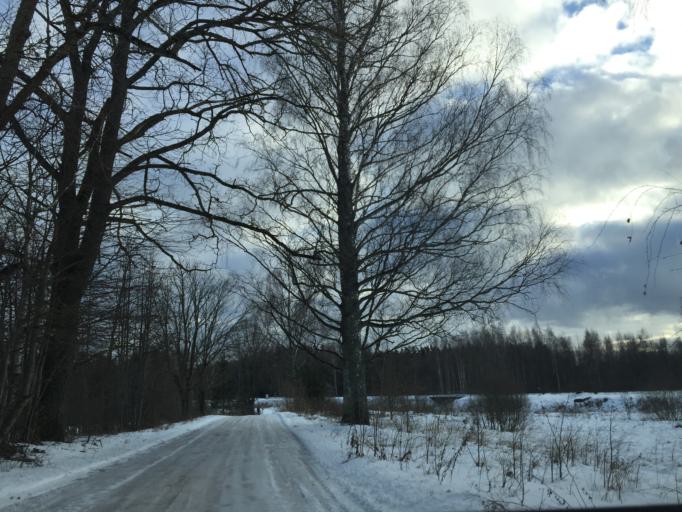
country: LV
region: Lielvarde
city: Lielvarde
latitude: 56.5757
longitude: 24.7968
